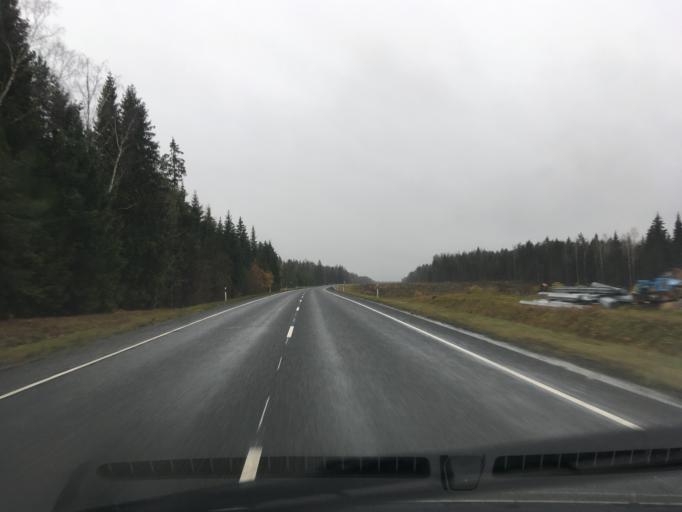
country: EE
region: Harju
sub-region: Nissi vald
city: Turba
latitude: 58.9695
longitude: 24.0652
